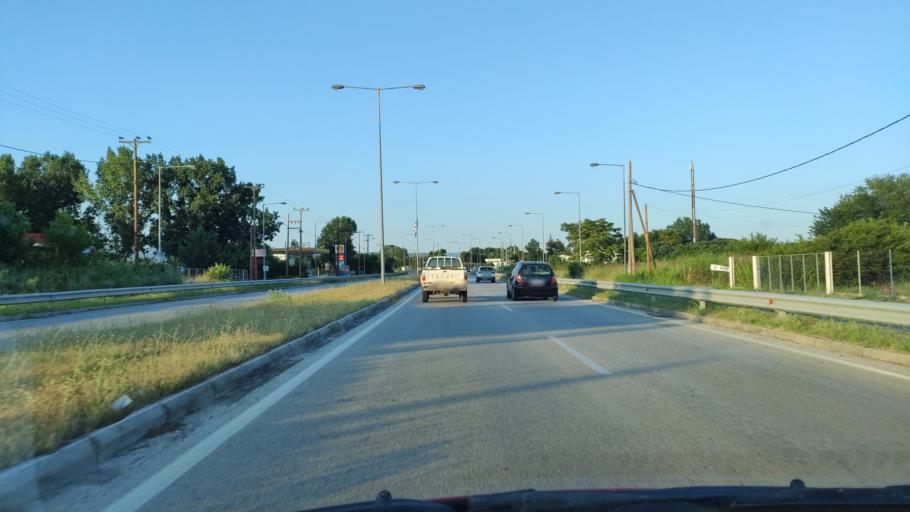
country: GR
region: East Macedonia and Thrace
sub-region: Nomos Rodopis
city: Komotini
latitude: 41.1133
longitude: 25.3770
